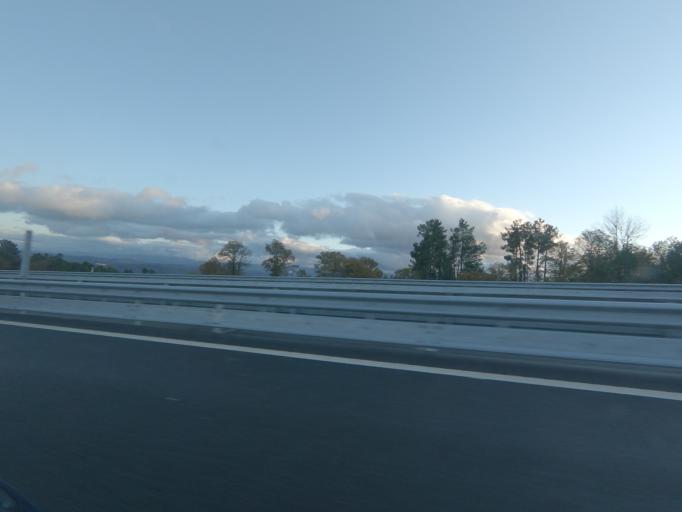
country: PT
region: Vila Real
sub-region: Santa Marta de Penaguiao
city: Santa Marta de Penaguiao
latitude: 41.2653
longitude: -7.8079
